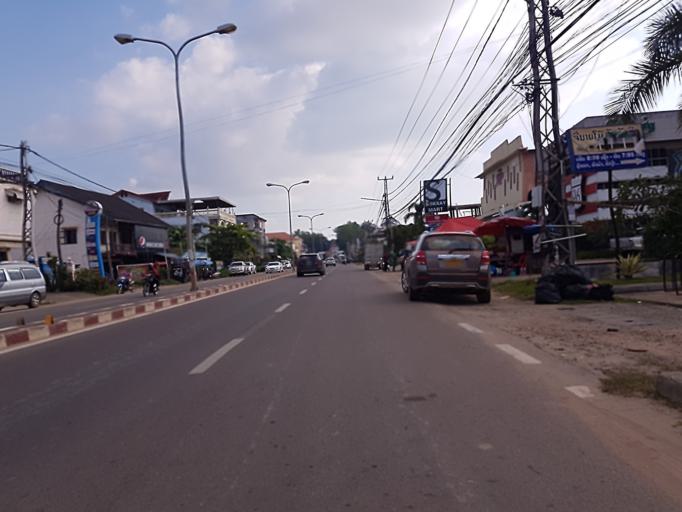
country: TH
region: Nong Khai
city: Si Chiang Mai
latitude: 17.9126
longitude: 102.6202
